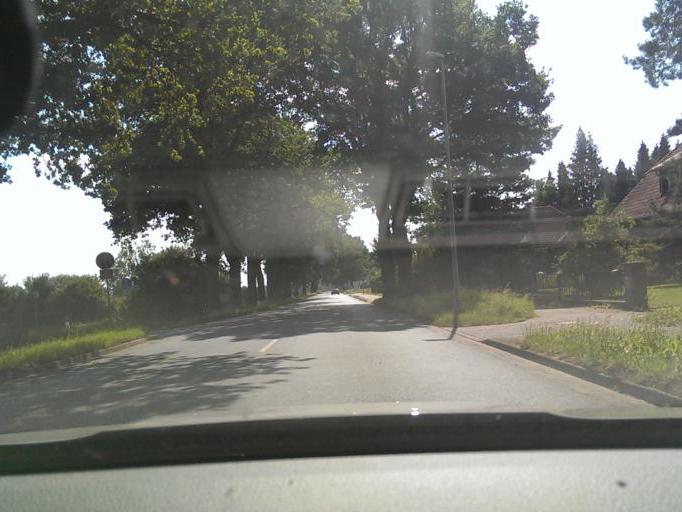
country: DE
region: Lower Saxony
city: Elze
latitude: 52.5414
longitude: 9.7282
